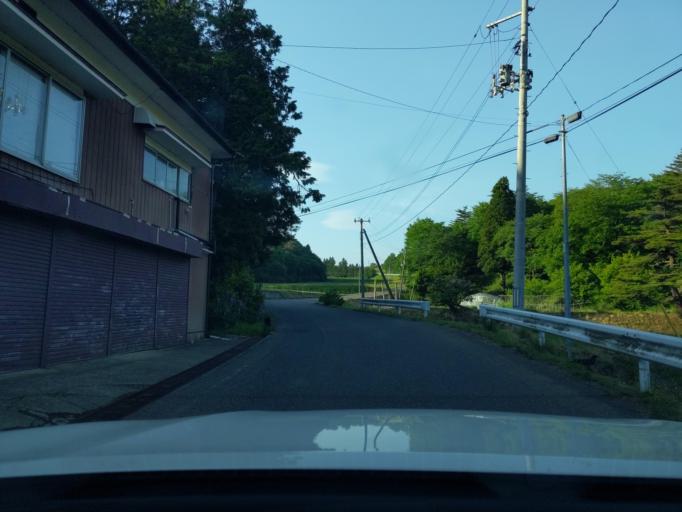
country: JP
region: Fukushima
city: Motomiya
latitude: 37.5244
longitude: 140.3331
